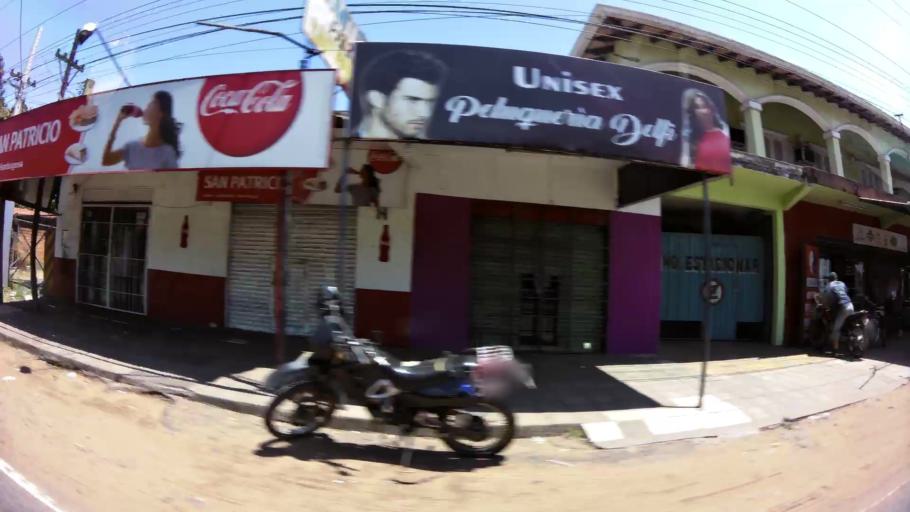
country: PY
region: Central
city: Nemby
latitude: -25.4055
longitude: -57.5425
